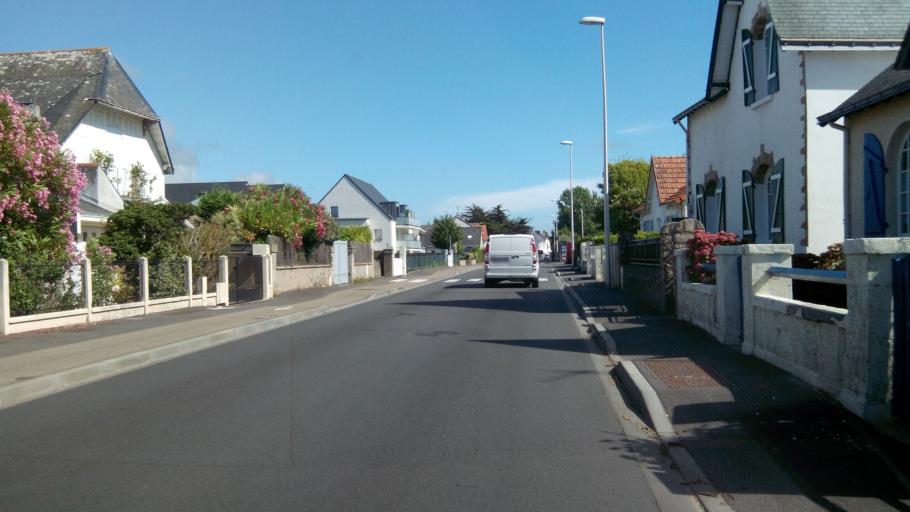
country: FR
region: Pays de la Loire
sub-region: Departement de la Loire-Atlantique
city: Le Croisic
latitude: 47.2900
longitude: -2.5134
